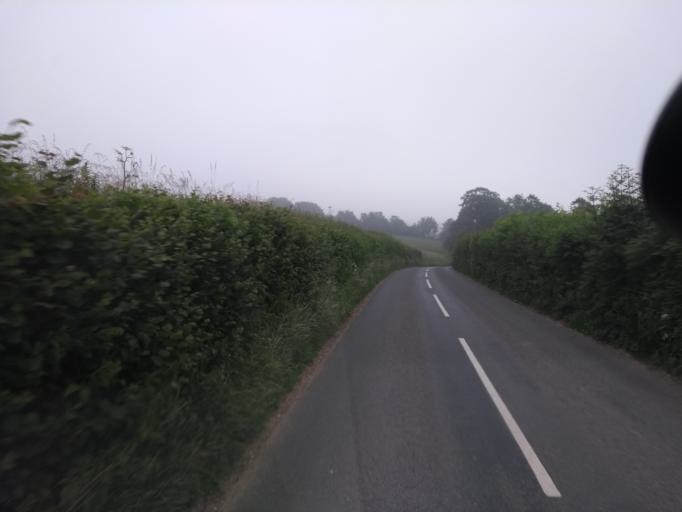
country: GB
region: England
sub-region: Somerset
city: Crewkerne
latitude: 50.8295
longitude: -2.8097
